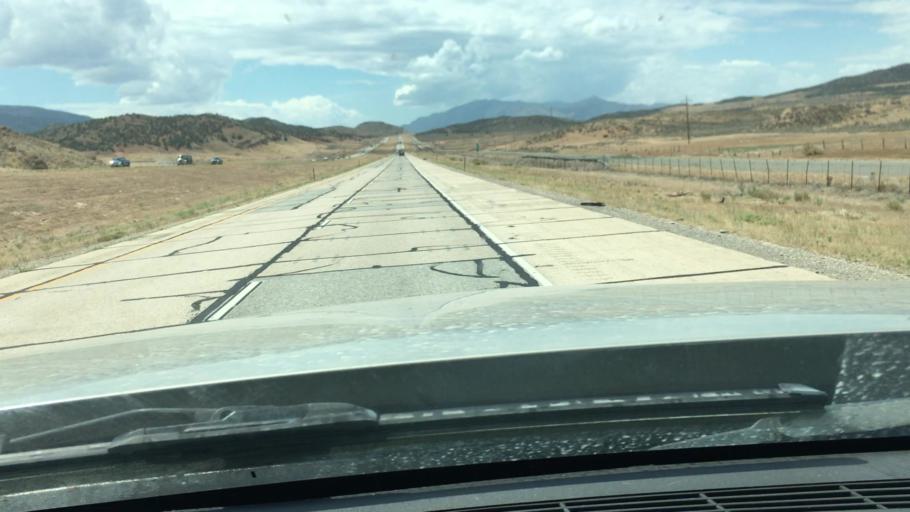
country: US
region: Utah
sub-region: Sanpete County
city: Gunnison
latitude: 39.3722
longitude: -112.0799
